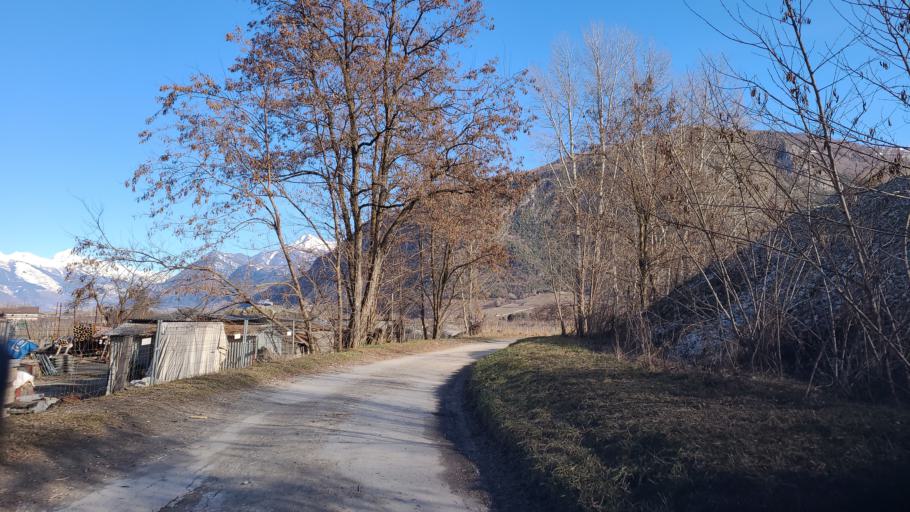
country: CH
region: Valais
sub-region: Sion District
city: Grimisuat
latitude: 46.2373
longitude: 7.3904
